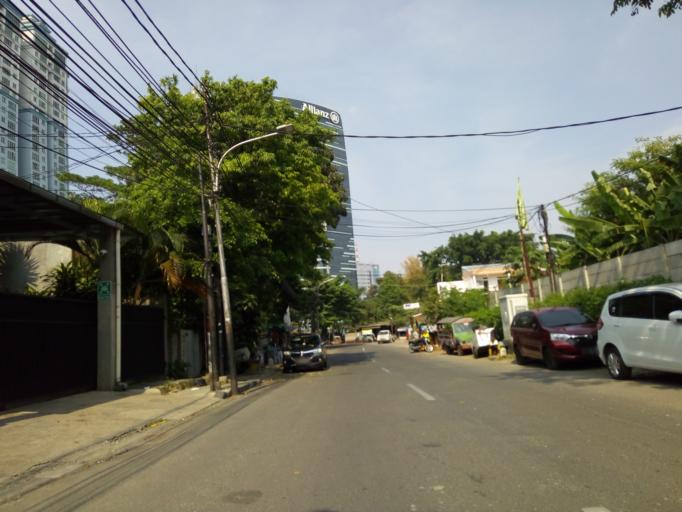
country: ID
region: Jakarta Raya
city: Jakarta
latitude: -6.2077
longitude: 106.8330
